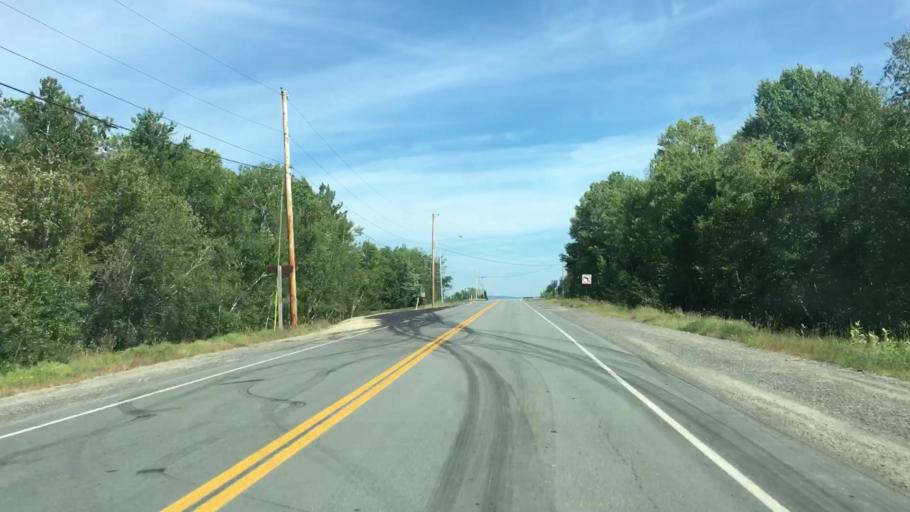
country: US
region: Maine
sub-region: Penobscot County
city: Howland
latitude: 45.2351
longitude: -68.6818
